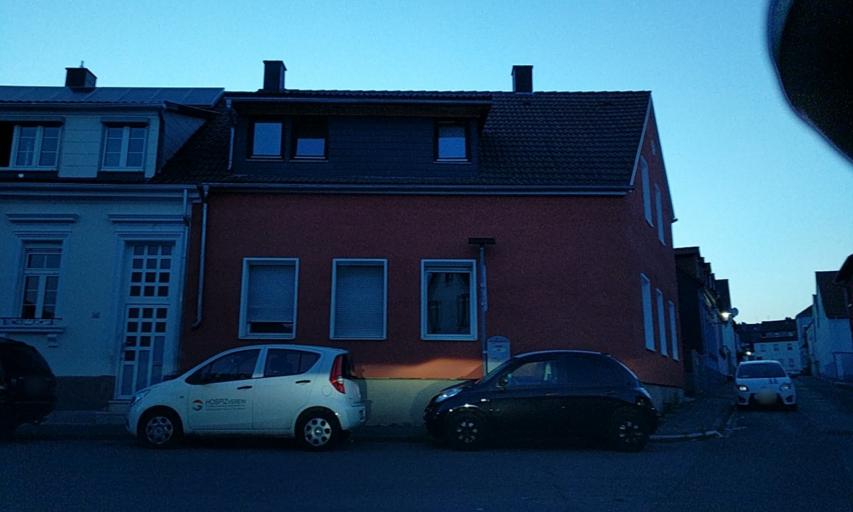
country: DE
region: Rheinland-Pfalz
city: Kaiserslautern
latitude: 49.4438
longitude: 7.7545
